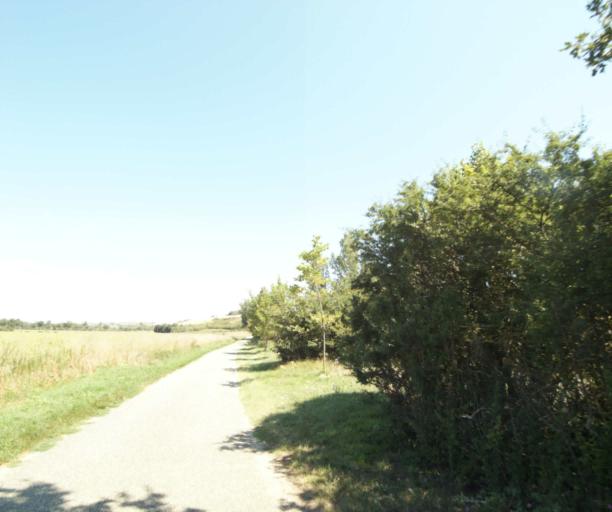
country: FR
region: Midi-Pyrenees
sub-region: Departement de l'Ariege
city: Lezat-sur-Leze
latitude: 43.2767
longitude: 1.3565
